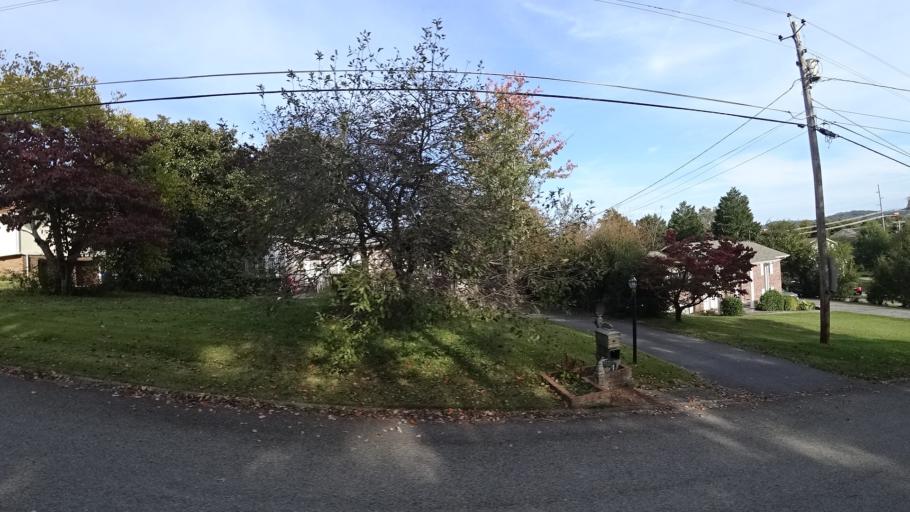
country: US
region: Tennessee
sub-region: Knox County
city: Farragut
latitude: 35.9118
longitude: -84.1588
